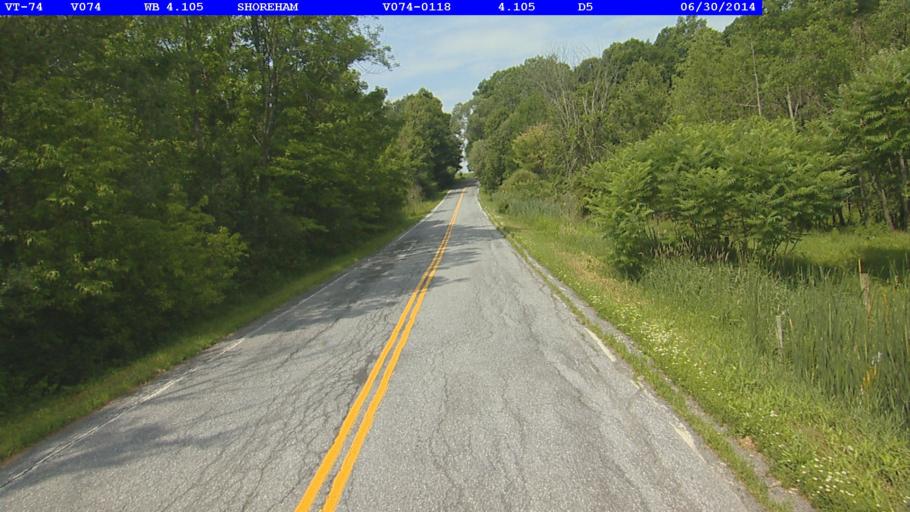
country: US
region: New York
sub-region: Essex County
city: Ticonderoga
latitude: 43.8857
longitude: -73.3259
